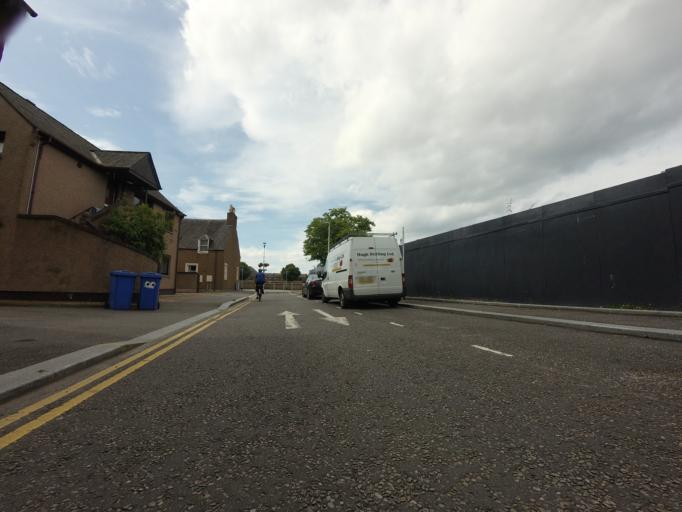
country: GB
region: Scotland
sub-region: Highland
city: Inverness
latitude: 57.4812
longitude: -4.2318
